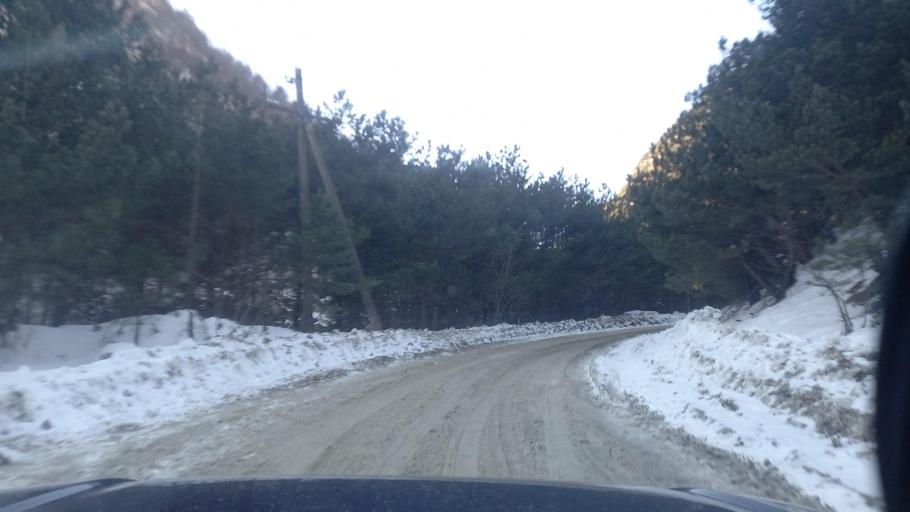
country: RU
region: Kabardino-Balkariya
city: Verkhnyaya Balkariya
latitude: 42.9014
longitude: 43.5968
